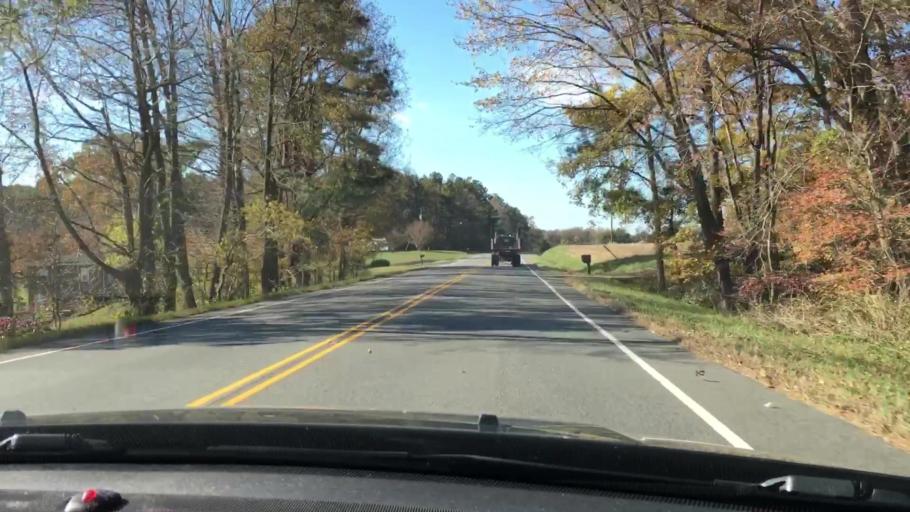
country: US
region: Virginia
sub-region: King William County
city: Central Garage
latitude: 37.7892
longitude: -77.1946
